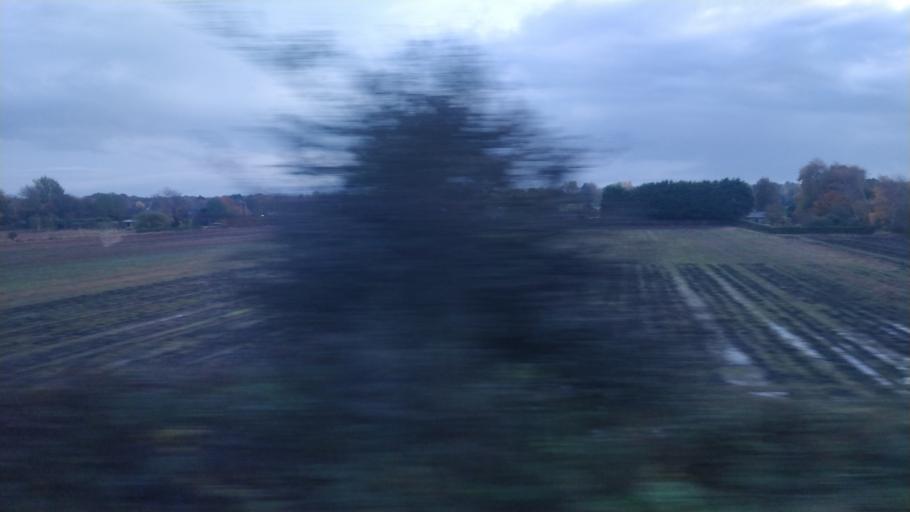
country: GB
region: England
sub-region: Lancashire
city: Parbold
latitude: 53.6029
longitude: -2.8287
